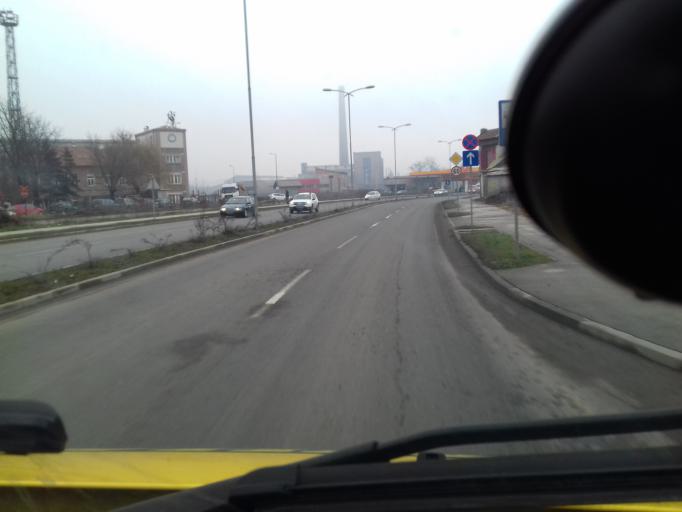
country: BA
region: Federation of Bosnia and Herzegovina
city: Zenica
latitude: 44.2080
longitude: 17.9023
